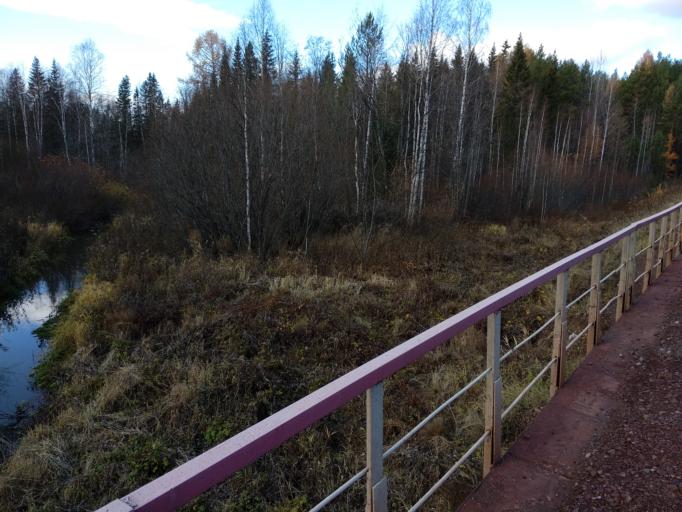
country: RU
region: Sverdlovsk
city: Volchansk
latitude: 59.8930
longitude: 60.1143
